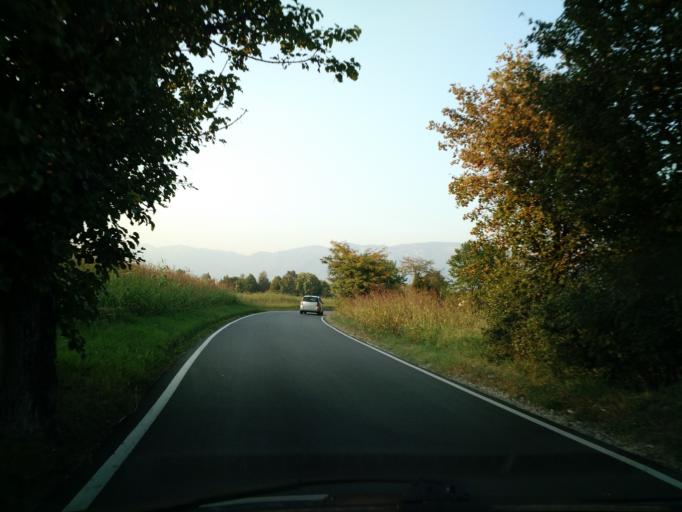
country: IT
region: Veneto
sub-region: Provincia di Vicenza
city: Thiene
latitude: 45.6929
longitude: 11.4752
